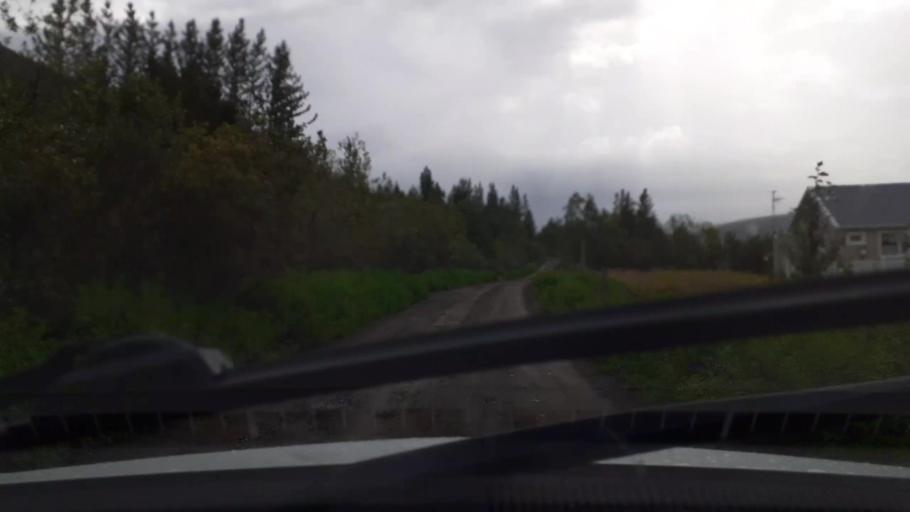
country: IS
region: Capital Region
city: Mosfellsbaer
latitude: 64.4970
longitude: -21.3572
